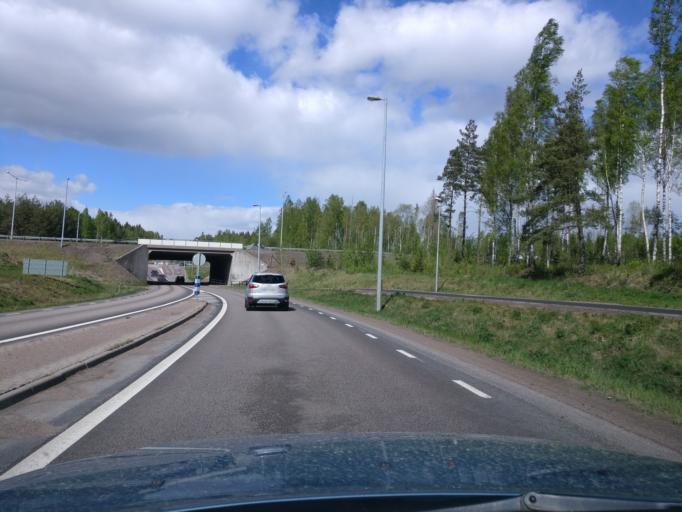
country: SE
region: Vaermland
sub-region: Karlstads Kommun
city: Skattkarr
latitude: 59.3973
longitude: 13.5833
